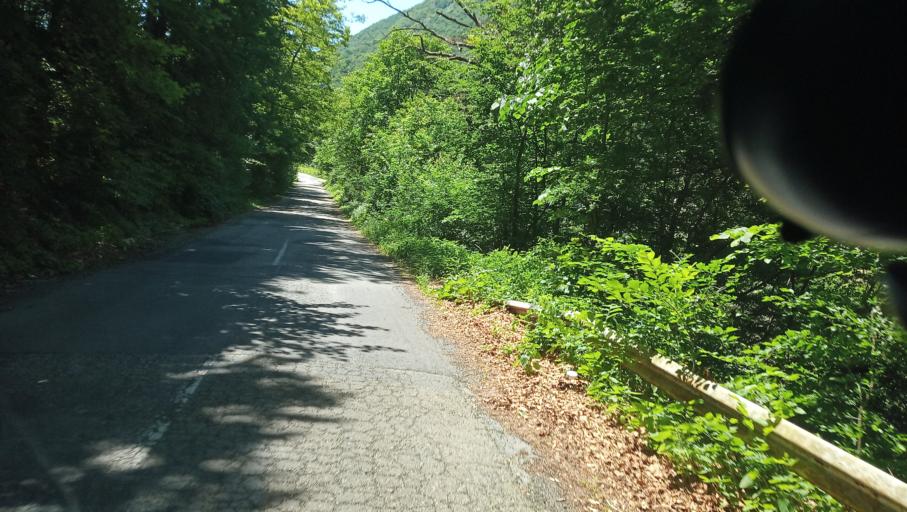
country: RO
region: Caras-Severin
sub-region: Comuna Mehadia
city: Valea Bolvasnita
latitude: 44.9654
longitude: 22.4862
